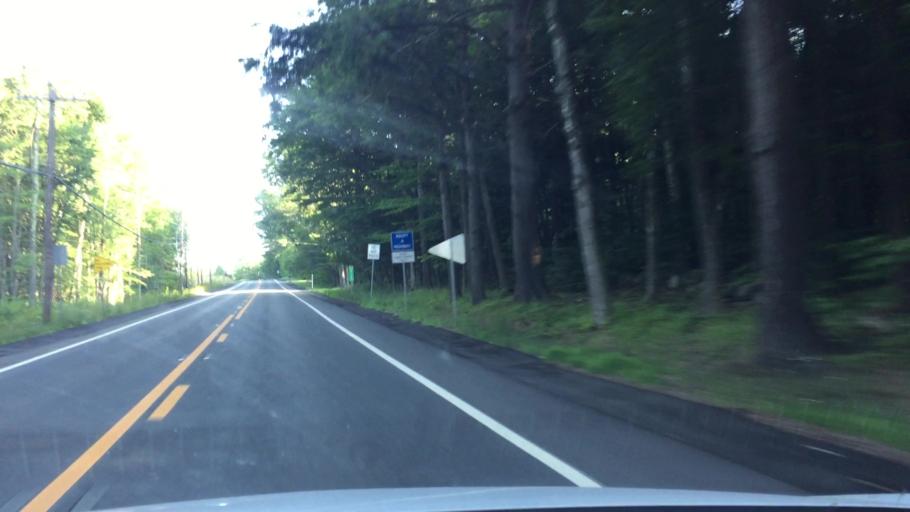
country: US
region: Massachusetts
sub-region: Berkshire County
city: Becket
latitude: 42.2711
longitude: -73.0538
